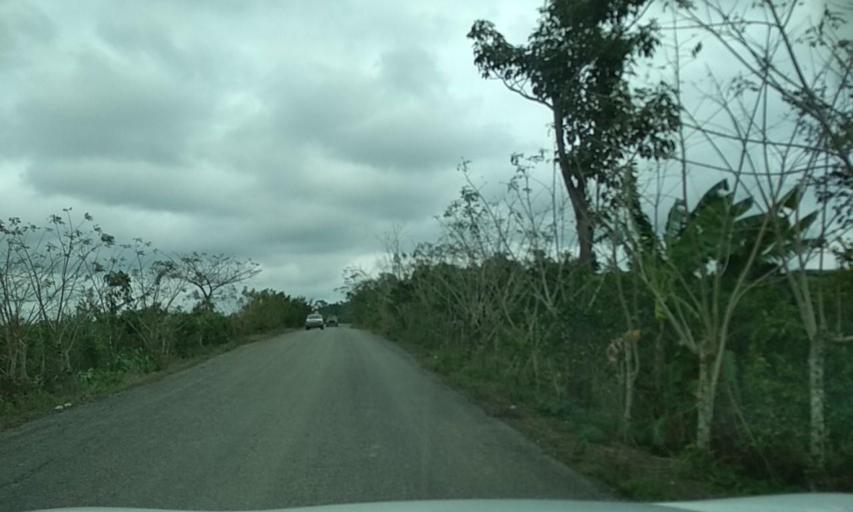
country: MX
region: Veracruz
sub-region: Coatzintla
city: Manuel Maria Contreras
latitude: 20.3399
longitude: -97.4639
